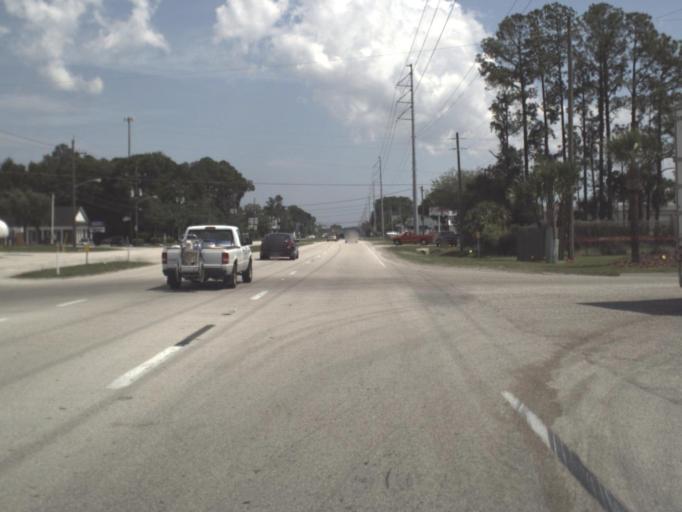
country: US
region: Florida
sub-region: Duval County
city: Jacksonville
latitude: 30.2592
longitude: -81.6130
